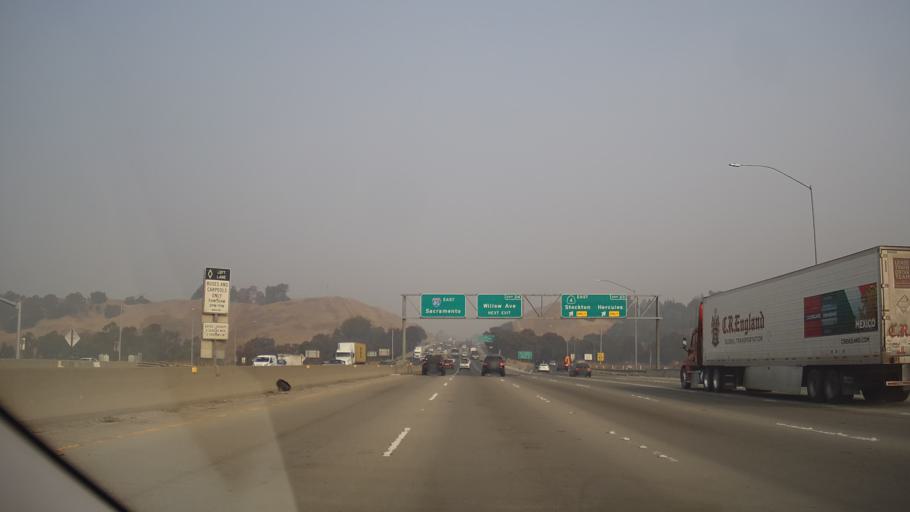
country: US
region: California
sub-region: Contra Costa County
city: Hercules
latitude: 38.0119
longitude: -122.2729
